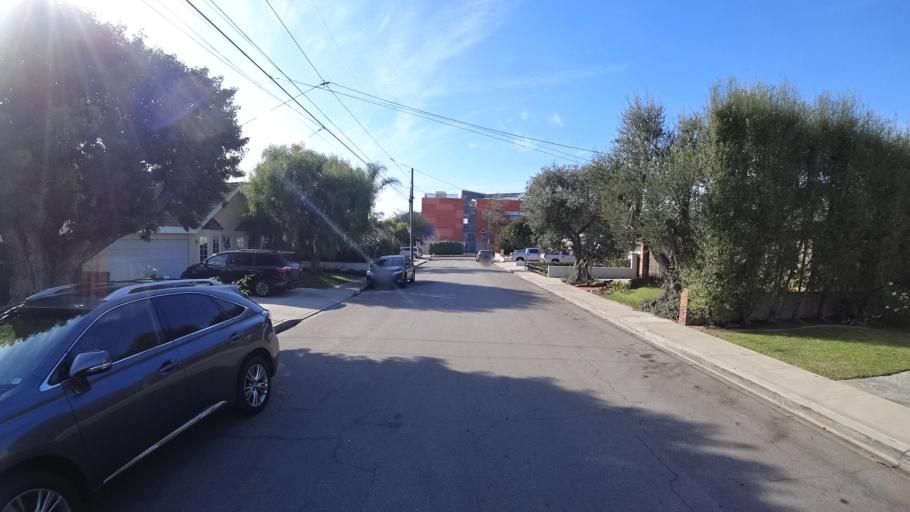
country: US
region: California
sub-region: Los Angeles County
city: Hermosa Beach
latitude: 33.8738
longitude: -118.3867
